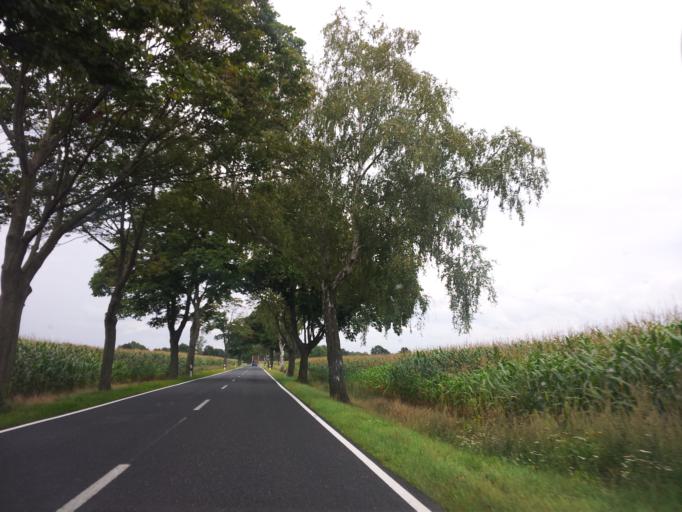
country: DE
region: Brandenburg
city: Gorzke
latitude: 52.1732
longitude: 12.3871
